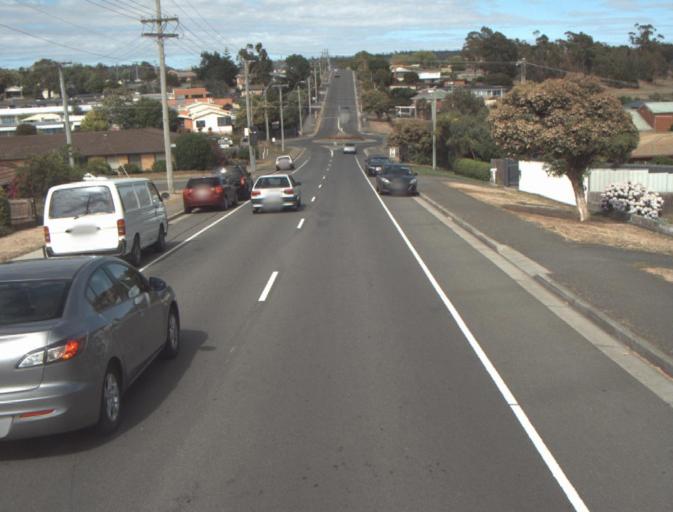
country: AU
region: Tasmania
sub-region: Launceston
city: Summerhill
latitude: -41.4663
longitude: 147.1312
